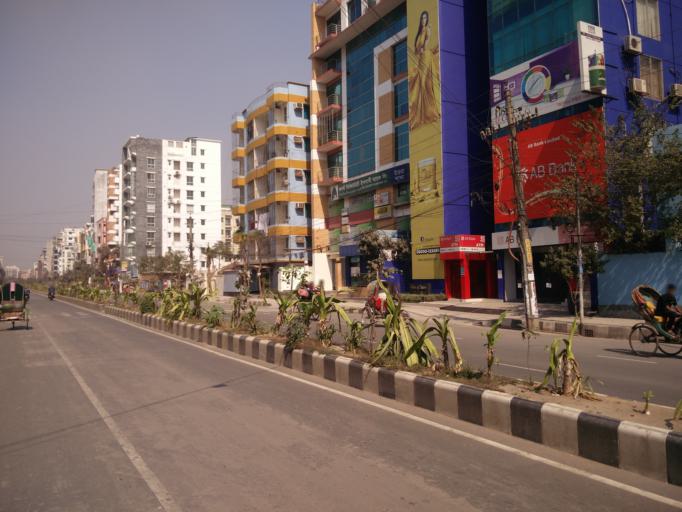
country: BD
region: Dhaka
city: Tungi
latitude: 23.8700
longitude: 90.3909
